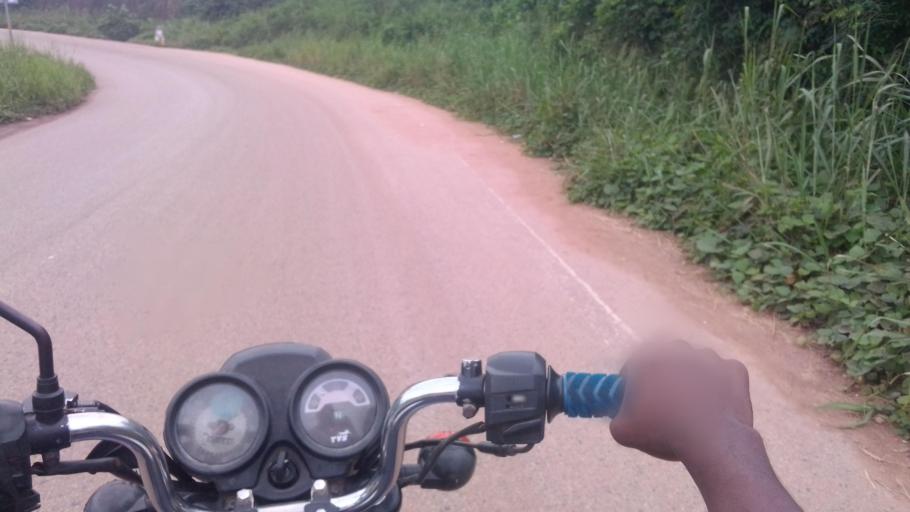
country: SL
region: Eastern Province
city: Kenema
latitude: 7.8762
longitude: -11.1749
